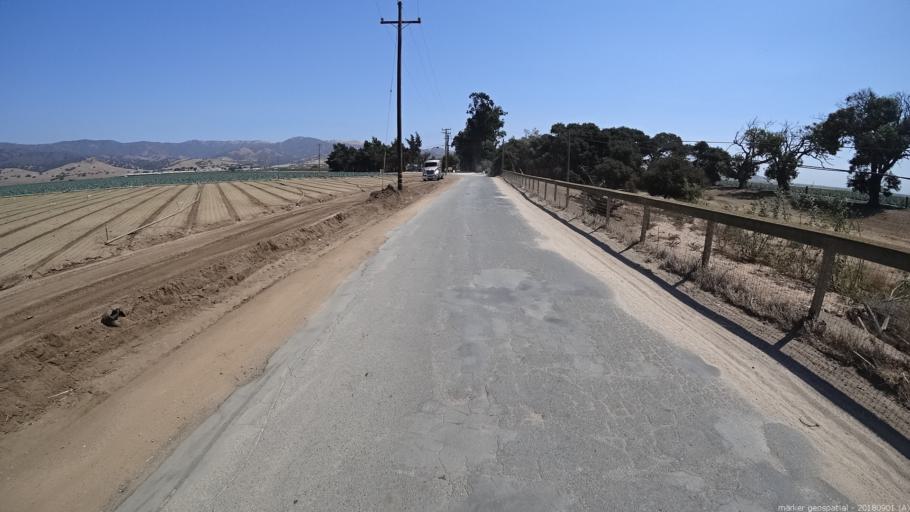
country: US
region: California
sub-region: Monterey County
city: Chualar
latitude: 36.6201
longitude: -121.5098
